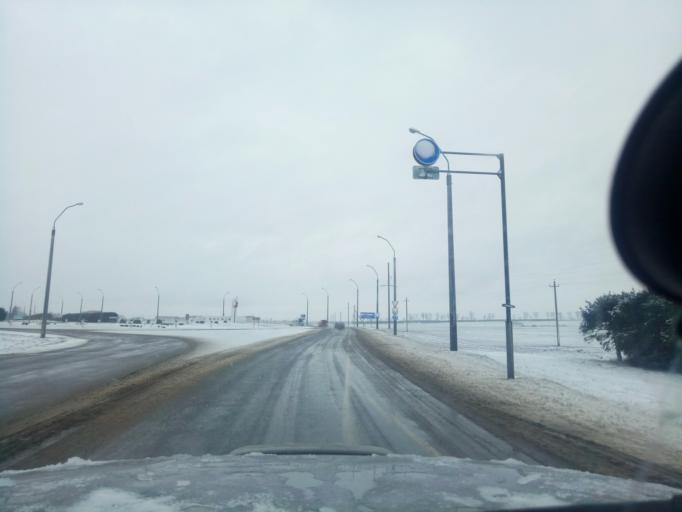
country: BY
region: Minsk
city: Nyasvizh
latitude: 53.2393
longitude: 26.6327
